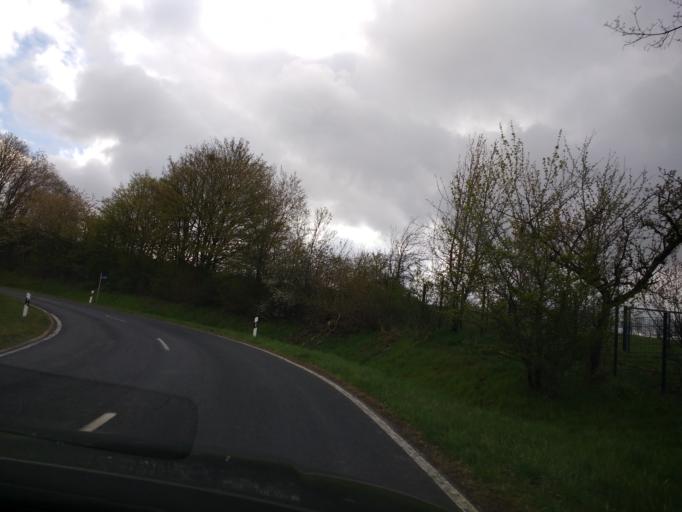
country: DE
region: Rheinland-Pfalz
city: Kopp
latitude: 50.1868
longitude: 6.5922
